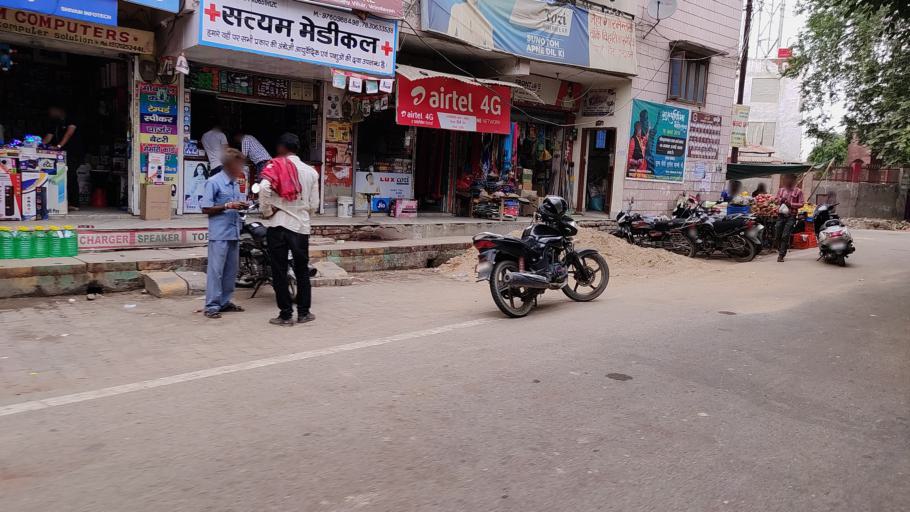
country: IN
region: Uttar Pradesh
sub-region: Mathura
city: Vrindavan
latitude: 27.5674
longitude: 77.6755
